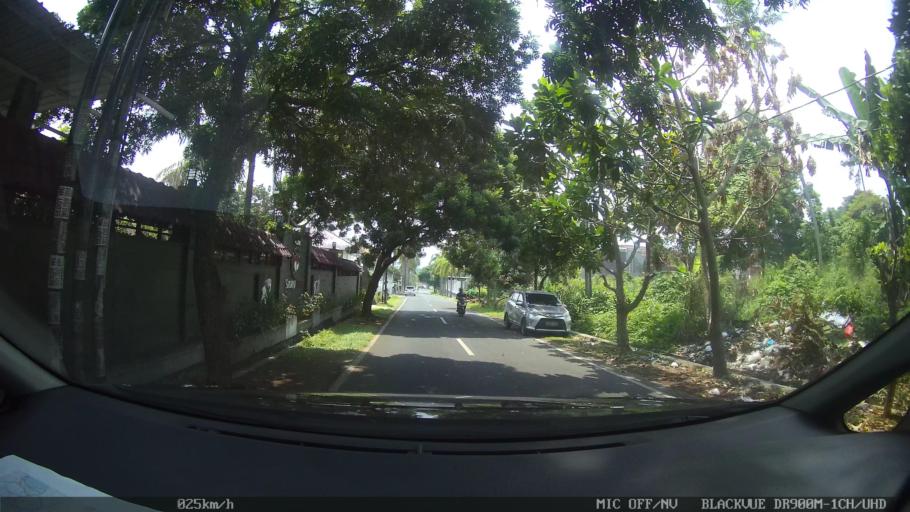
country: ID
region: Lampung
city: Bandarlampung
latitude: -5.4257
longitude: 105.2633
